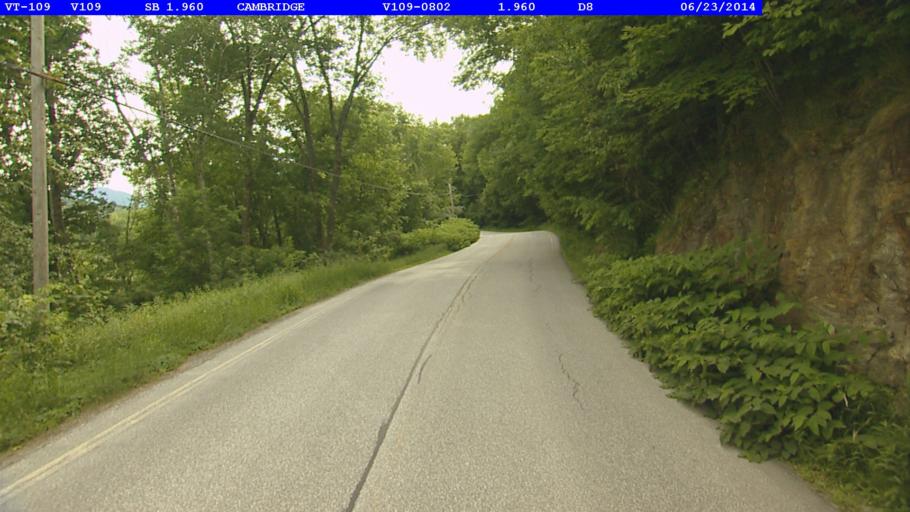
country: US
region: Vermont
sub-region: Lamoille County
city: Johnson
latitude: 44.6668
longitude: -72.7992
